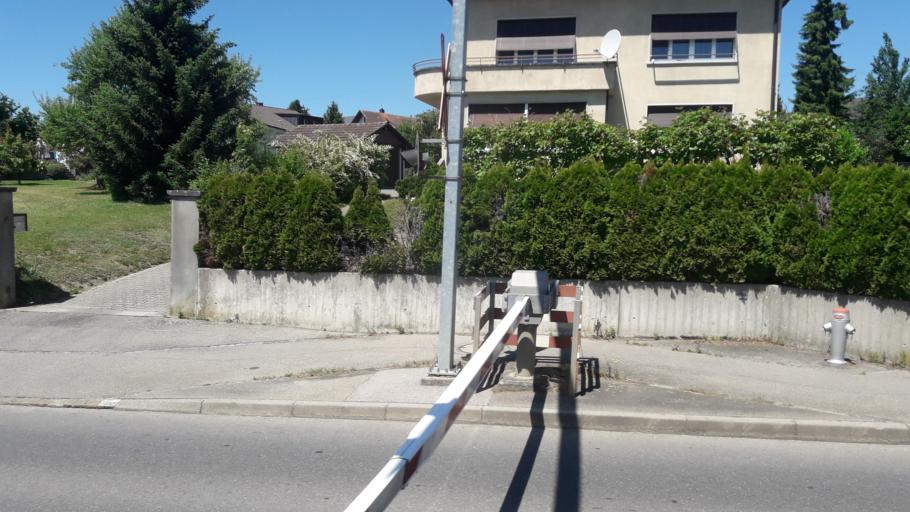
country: CH
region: Bern
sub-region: Seeland District
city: Tauffelen
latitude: 47.0601
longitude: 7.1901
